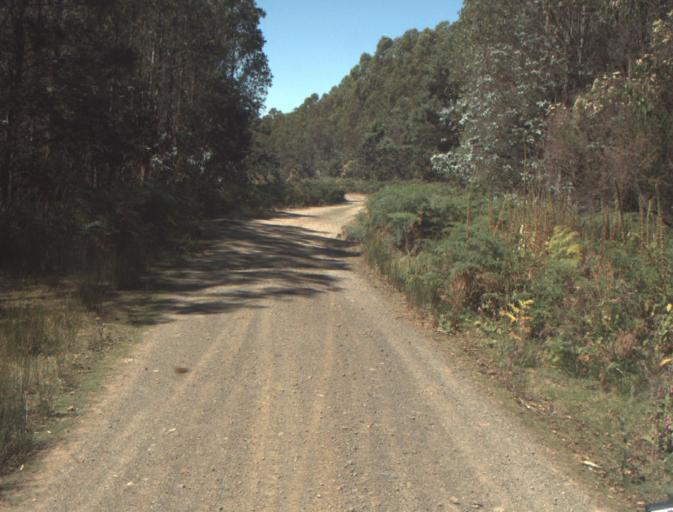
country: AU
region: Tasmania
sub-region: Dorset
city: Scottsdale
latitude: -41.2543
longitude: 147.3455
